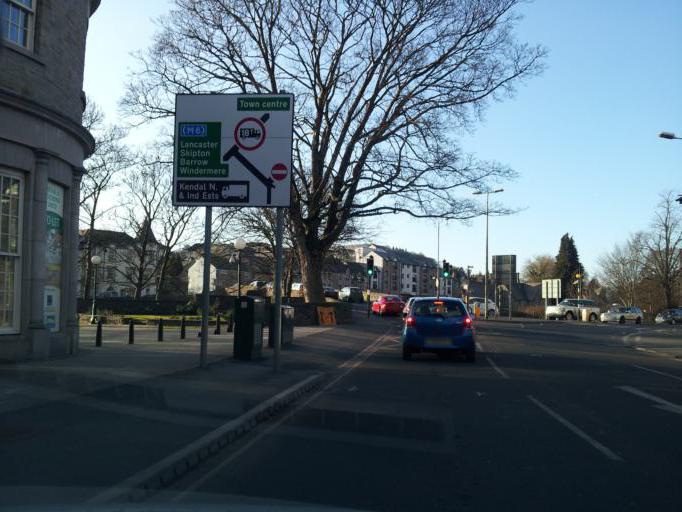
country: GB
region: England
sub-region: Cumbria
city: Kendal
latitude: 54.3202
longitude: -2.7436
